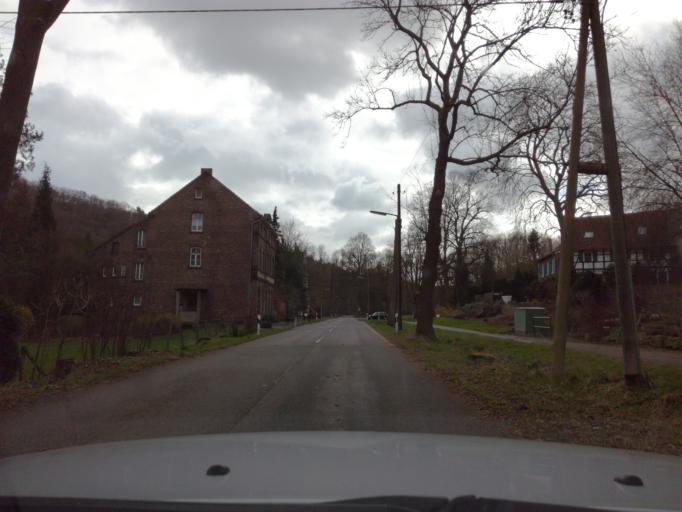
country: DE
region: North Rhine-Westphalia
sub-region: Regierungsbezirk Dusseldorf
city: Velbert
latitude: 51.3780
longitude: 7.0387
